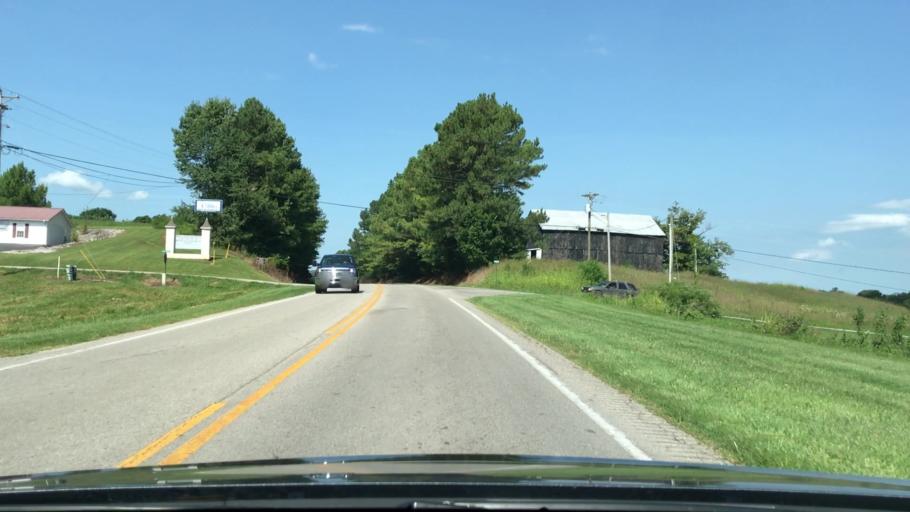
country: US
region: Kentucky
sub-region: Metcalfe County
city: Edmonton
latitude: 36.9888
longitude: -85.6392
